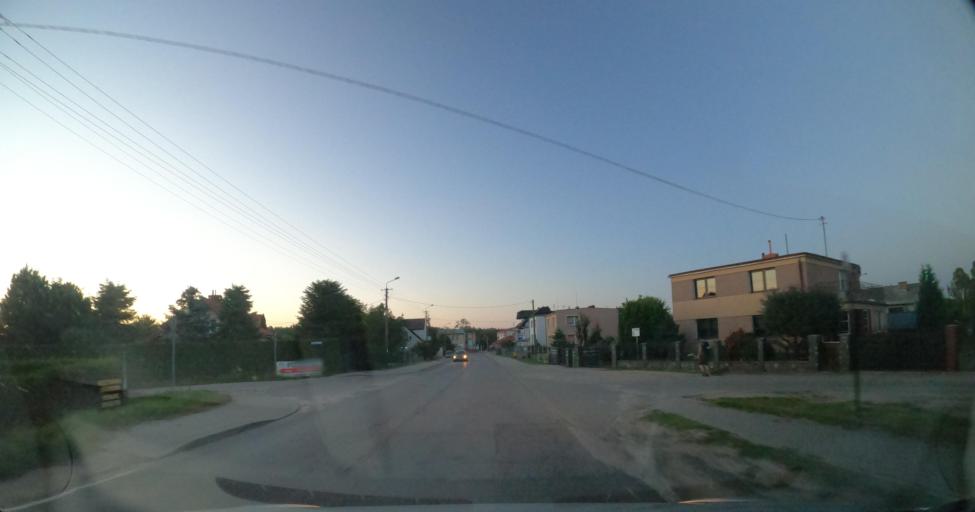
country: PL
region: Pomeranian Voivodeship
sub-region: Powiat wejherowski
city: Szemud
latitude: 54.4855
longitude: 18.2191
